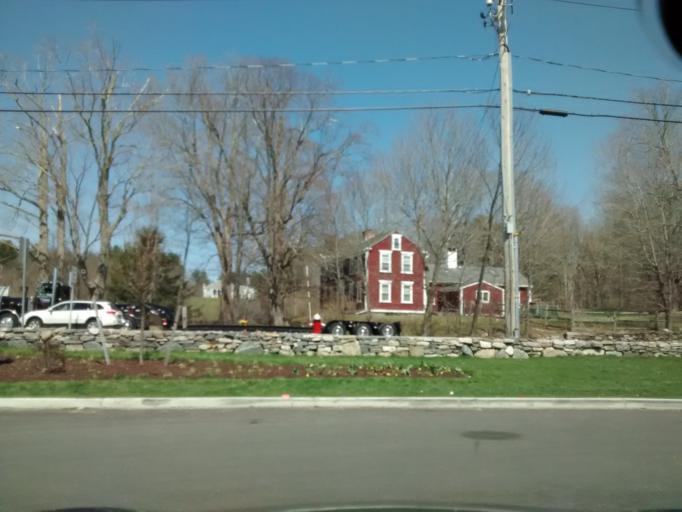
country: US
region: Massachusetts
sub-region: Worcester County
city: Oxford
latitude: 42.1148
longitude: -71.8480
